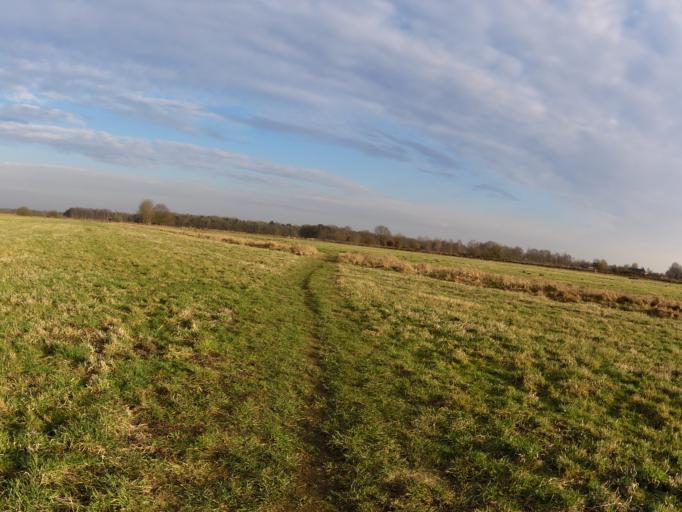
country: NL
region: North Brabant
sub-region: Gemeente Haaren
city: Haaren
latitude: 51.6437
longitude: 5.1740
